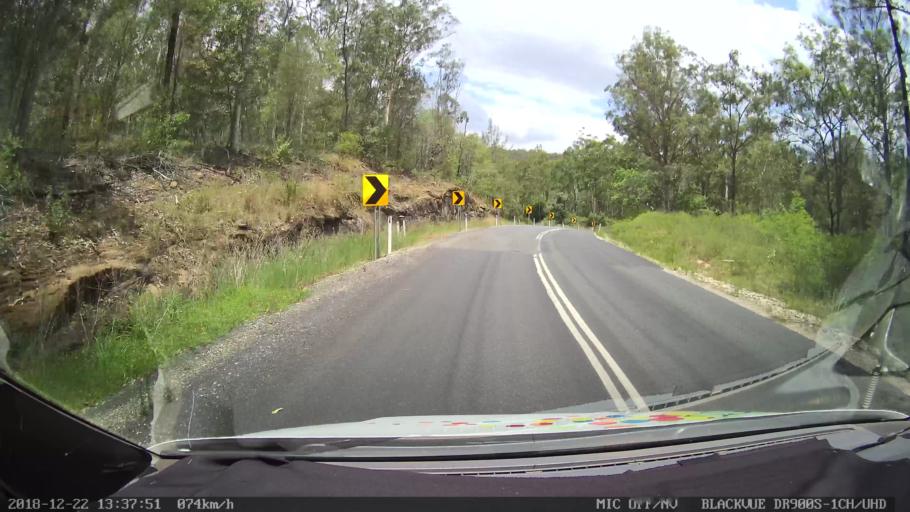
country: AU
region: New South Wales
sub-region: Clarence Valley
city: Coutts Crossing
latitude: -29.8943
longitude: 152.7900
